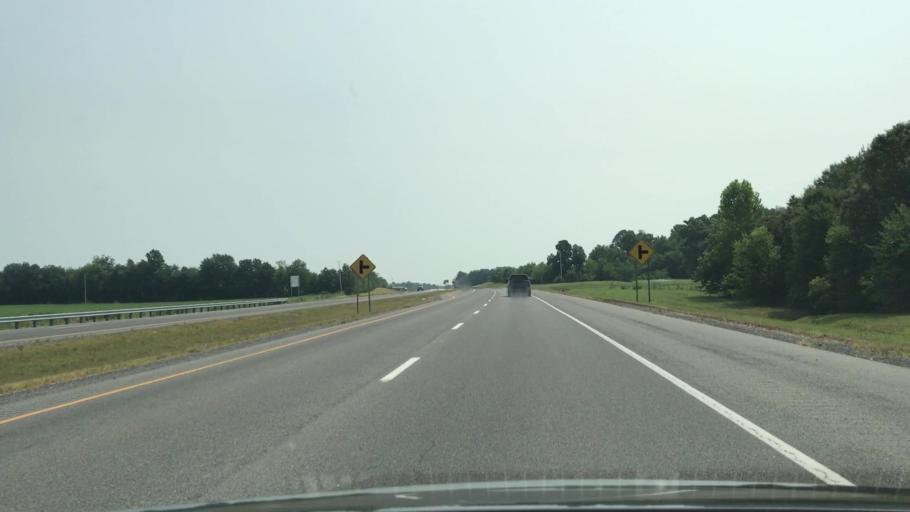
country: US
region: Kentucky
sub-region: Calloway County
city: Murray
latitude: 36.6492
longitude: -88.2403
